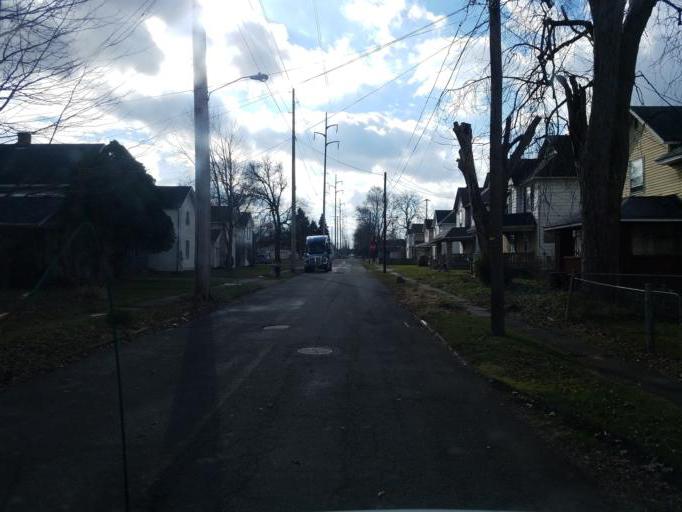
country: US
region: Ohio
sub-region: Marion County
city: Marion
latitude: 40.5842
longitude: -83.1455
